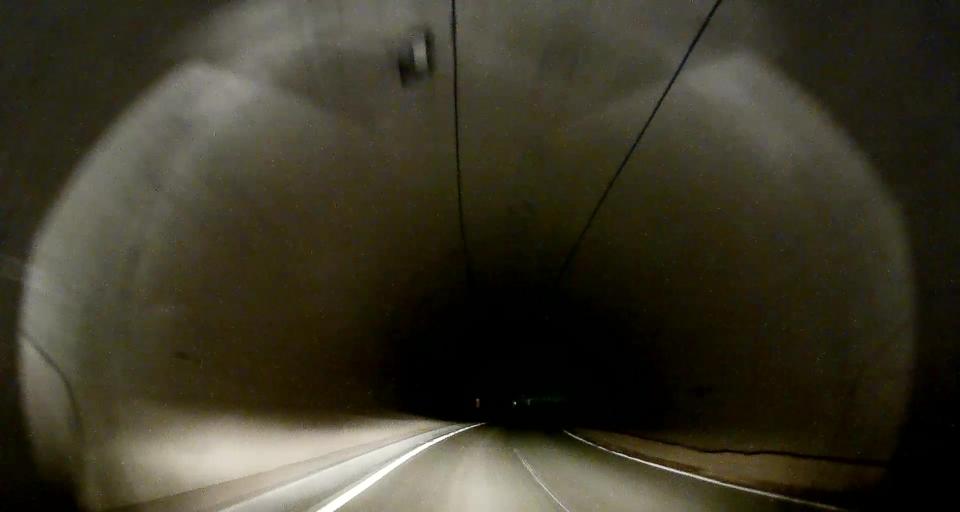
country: JP
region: Hokkaido
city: Chitose
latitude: 42.7892
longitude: 142.0442
